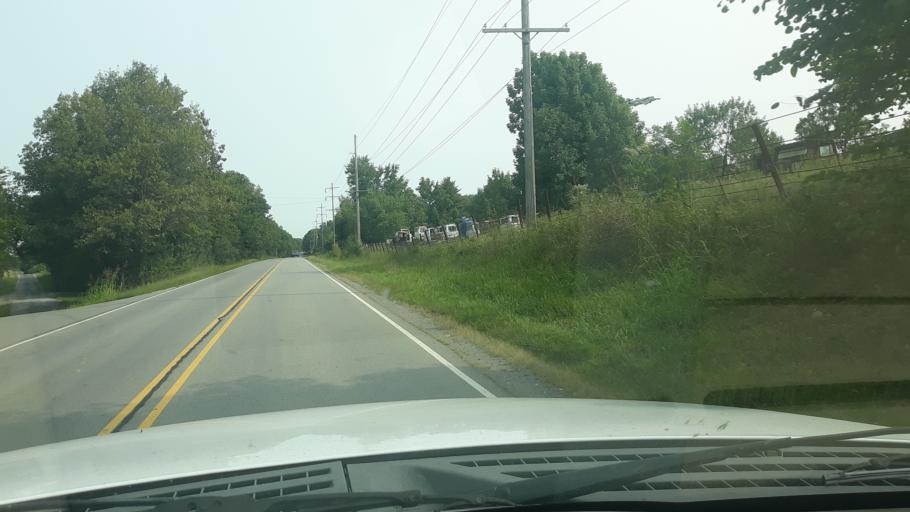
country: US
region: Illinois
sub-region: White County
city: Norris City
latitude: 37.9530
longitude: -88.3379
